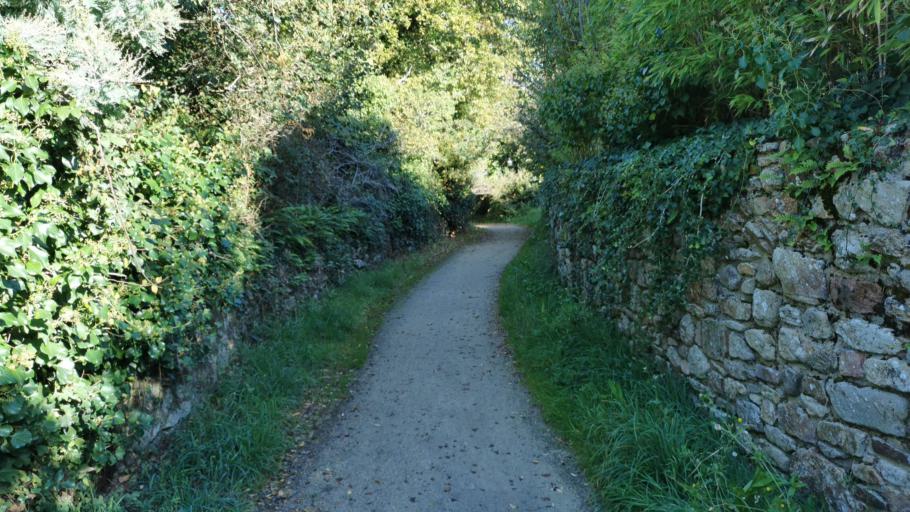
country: FR
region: Brittany
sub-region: Departement du Morbihan
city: Saint-Gildas-de-Rhuys
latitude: 47.5352
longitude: -2.8525
